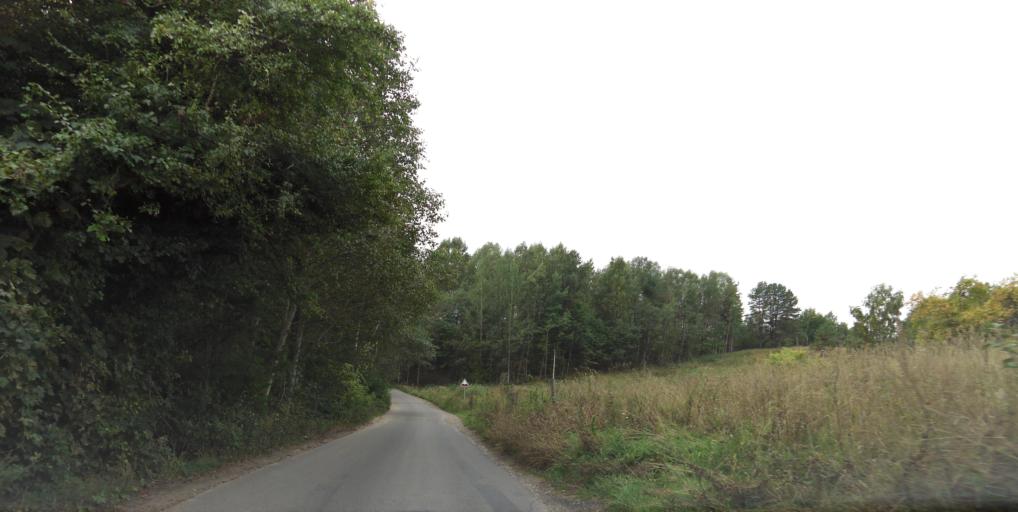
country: LT
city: Grigiskes
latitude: 54.7604
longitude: 25.0385
